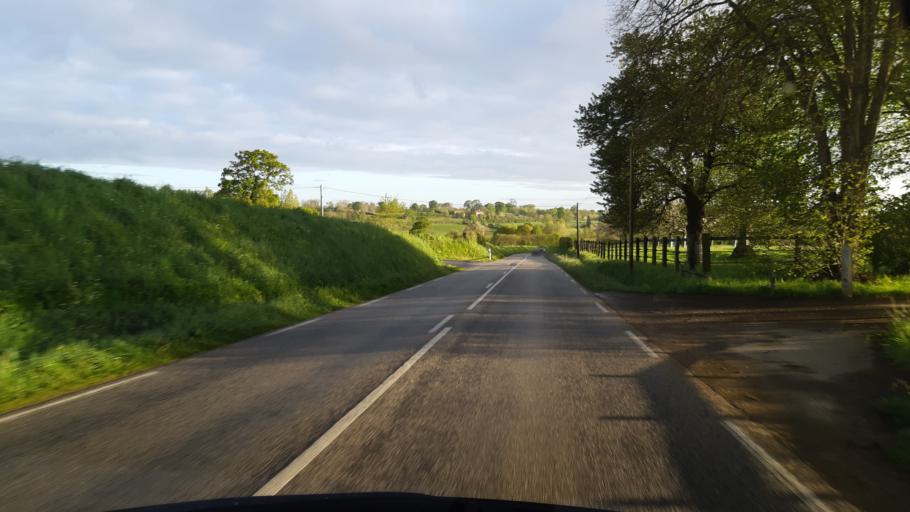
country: FR
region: Lower Normandy
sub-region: Departement de la Manche
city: Agneaux
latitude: 49.0638
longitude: -1.1324
